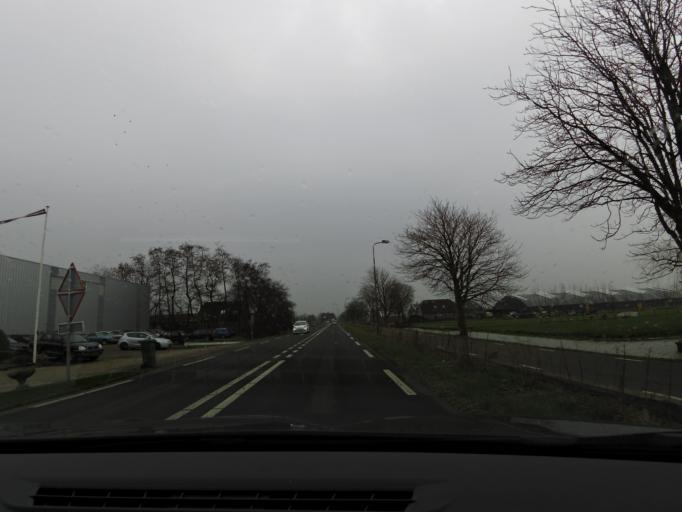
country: NL
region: South Holland
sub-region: Gemeente Nieuwkoop
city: Nieuwkoop
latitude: 52.1623
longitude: 4.7784
